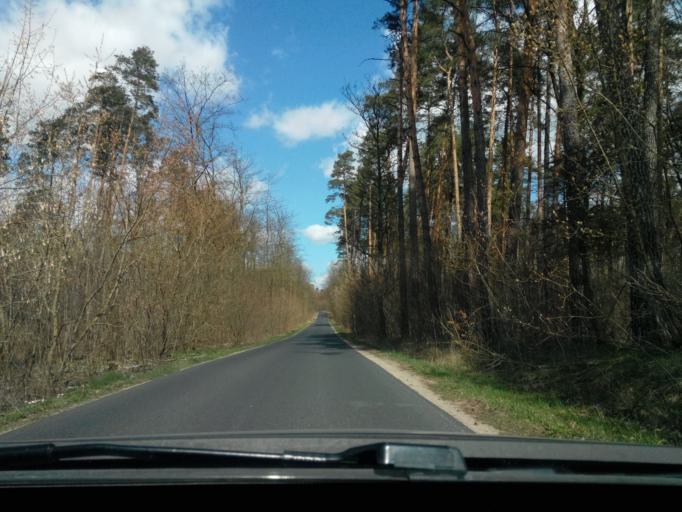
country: PL
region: Warmian-Masurian Voivodeship
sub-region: Powiat nowomiejski
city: Biskupiec
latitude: 53.4497
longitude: 19.3272
